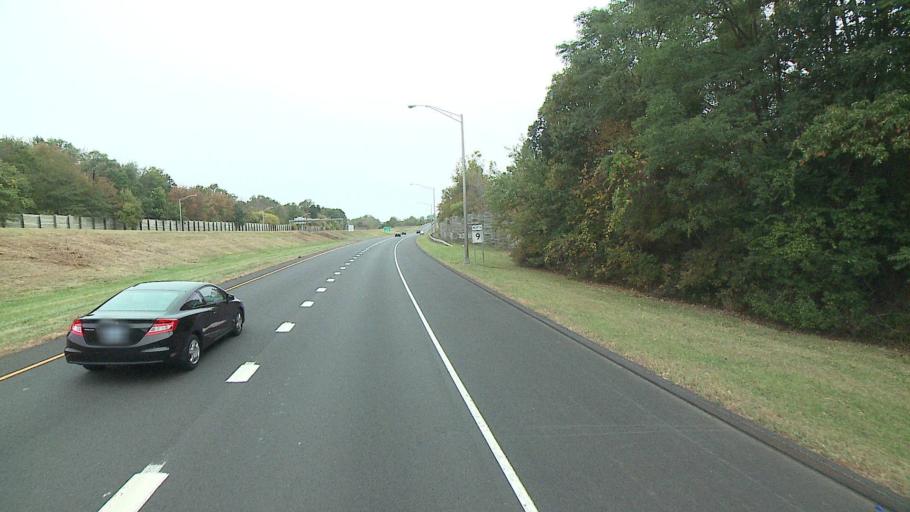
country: US
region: Connecticut
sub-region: Hartford County
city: Newington
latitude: 41.7185
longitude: -72.7702
